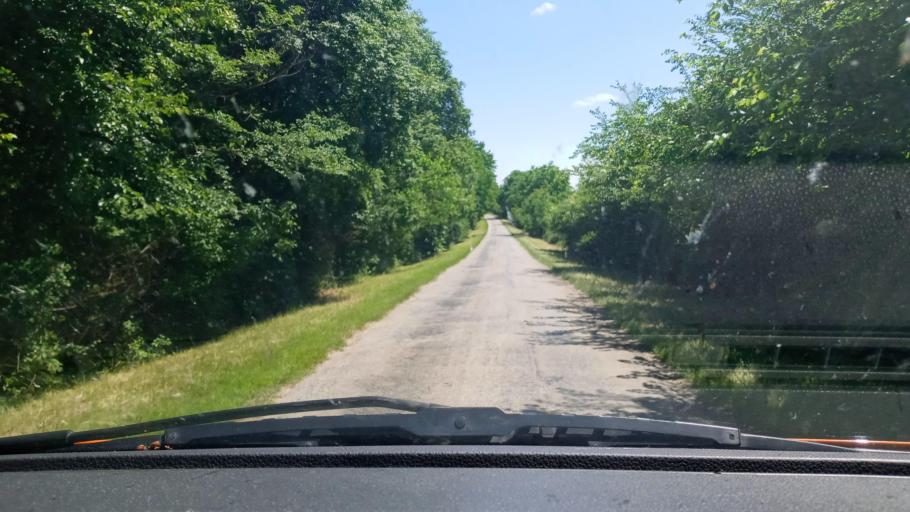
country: HU
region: Somogy
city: Kadarkut
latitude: 46.1810
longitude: 17.7378
